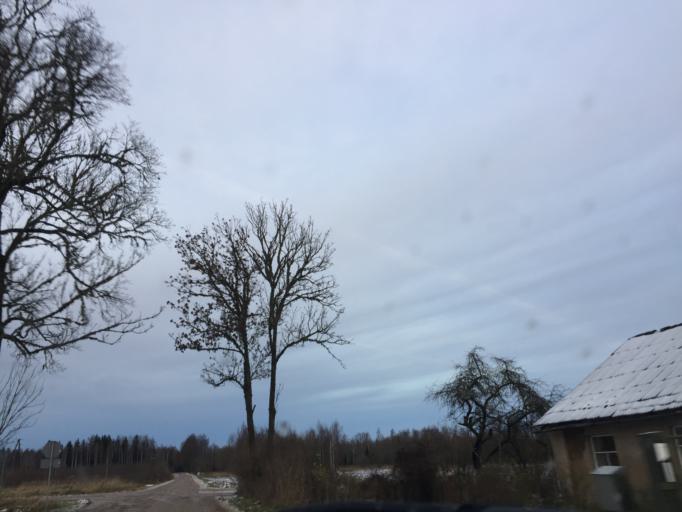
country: LV
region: Limbazu Rajons
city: Limbazi
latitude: 57.5528
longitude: 24.8155
